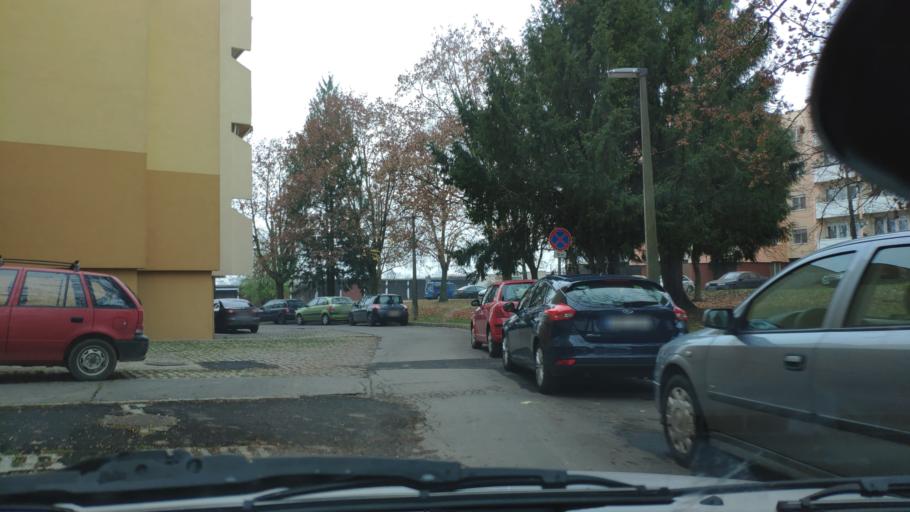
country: HU
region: Zala
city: Nagykanizsa
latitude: 46.4580
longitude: 17.0152
